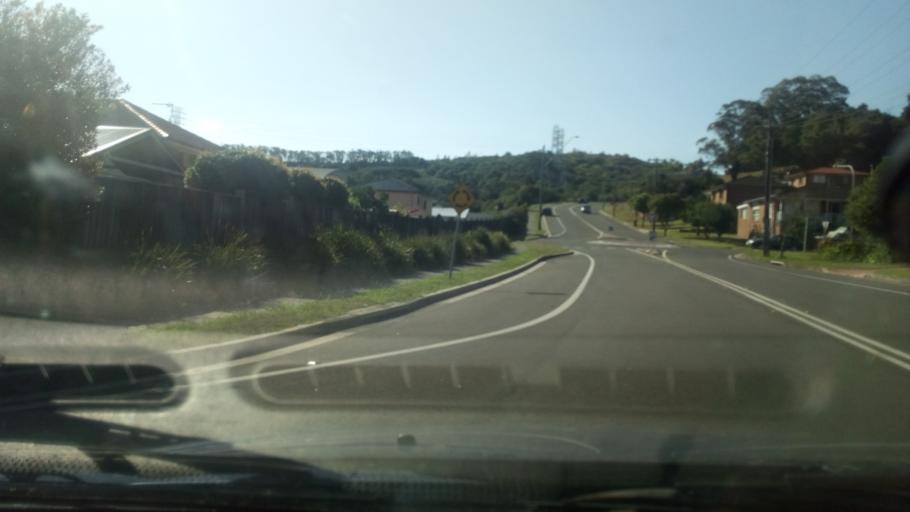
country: AU
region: New South Wales
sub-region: Wollongong
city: Berkeley
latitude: -34.4731
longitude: 150.8538
